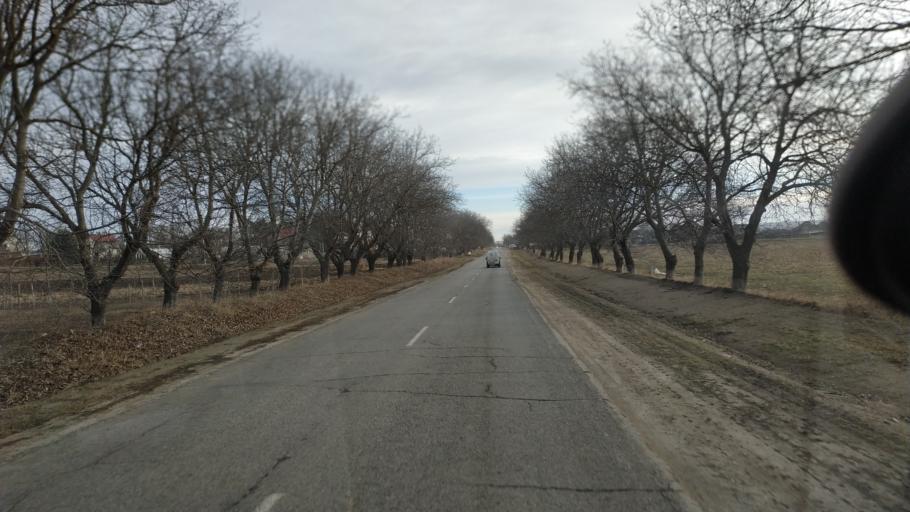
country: MD
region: Criuleni
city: Criuleni
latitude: 47.1579
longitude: 29.1099
